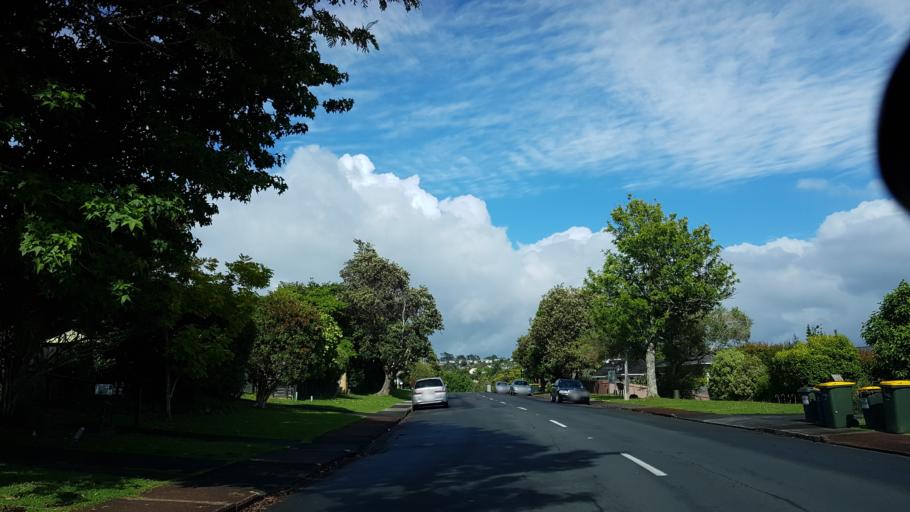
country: NZ
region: Auckland
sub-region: Auckland
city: North Shore
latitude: -36.7963
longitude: 174.7398
